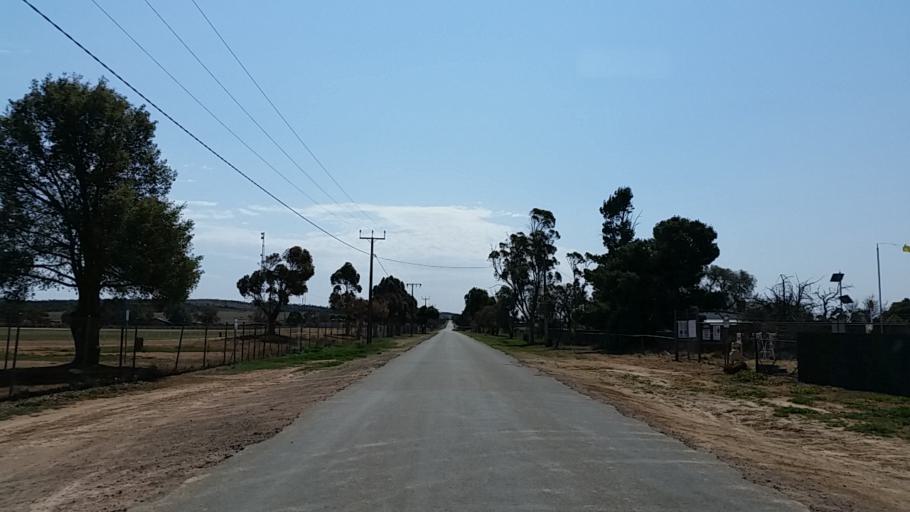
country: AU
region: South Australia
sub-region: Peterborough
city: Peterborough
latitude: -32.9718
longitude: 138.8466
